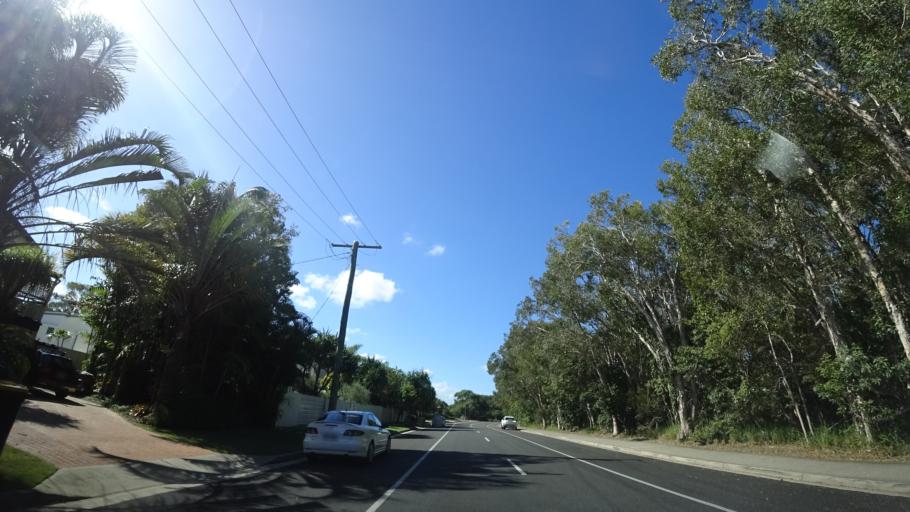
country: AU
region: Queensland
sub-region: Sunshine Coast
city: Mooloolaba
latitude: -26.6117
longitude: 153.0995
